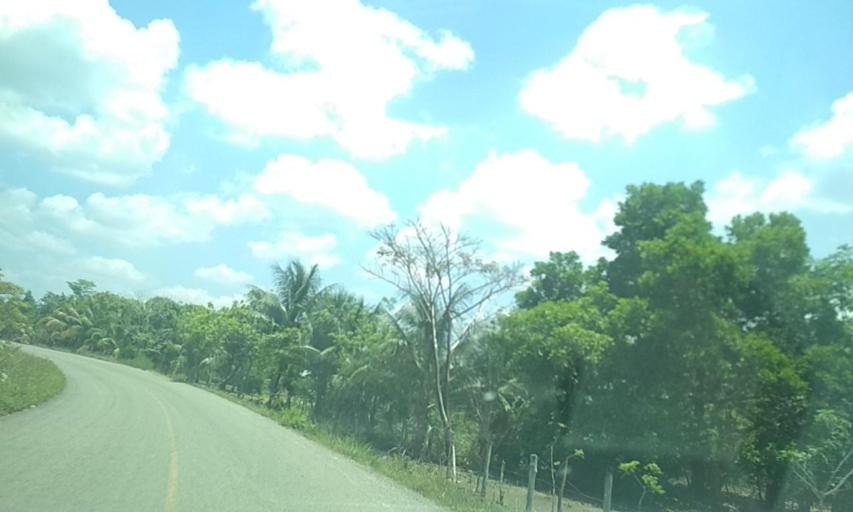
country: MX
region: Tabasco
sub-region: Huimanguillo
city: Francisco Rueda
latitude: 17.7917
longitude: -93.8500
